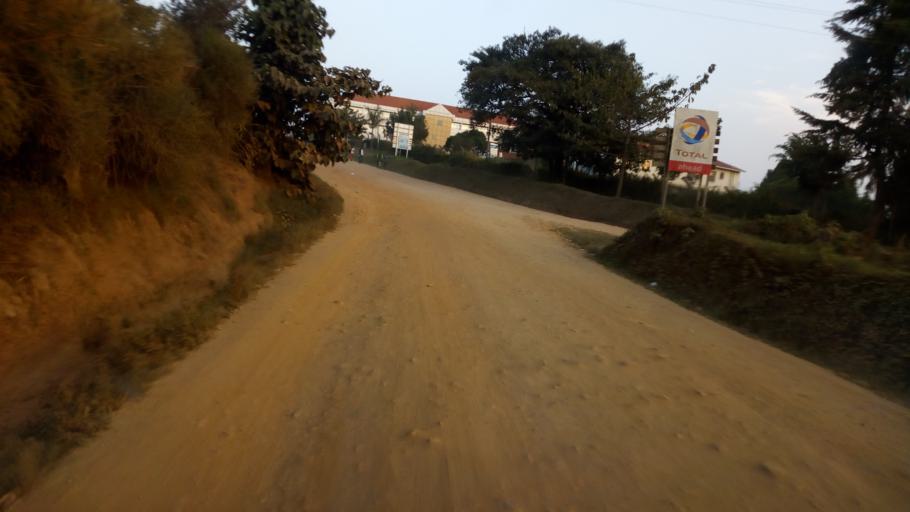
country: UG
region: Western Region
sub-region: Rukungiri District
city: Rukungiri
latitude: -0.7829
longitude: 29.9255
